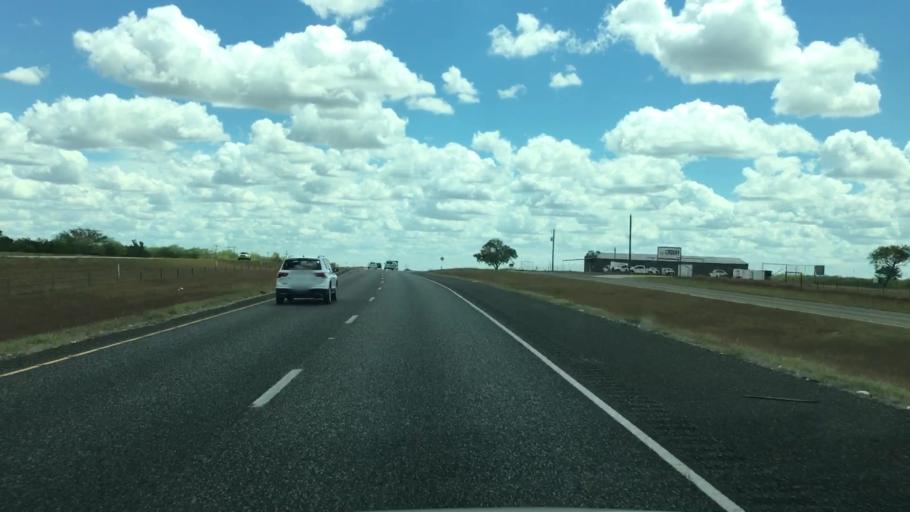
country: US
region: Texas
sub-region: Atascosa County
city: Pleasanton
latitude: 28.8708
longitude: -98.3949
